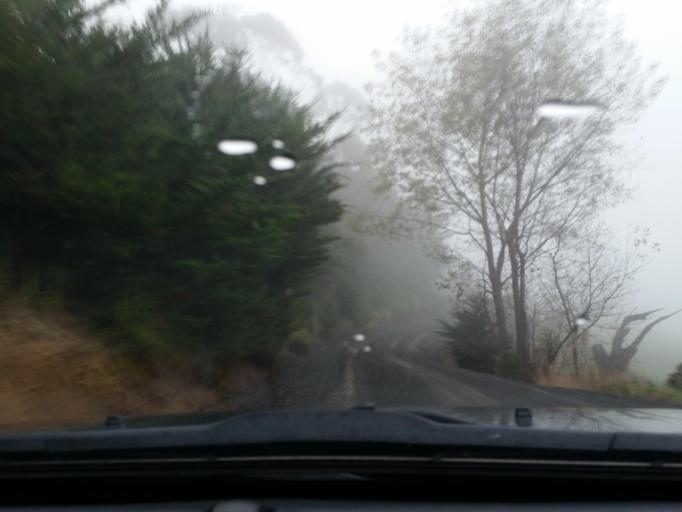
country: NZ
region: Northland
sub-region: Kaipara District
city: Dargaville
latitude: -35.9338
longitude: 173.9781
